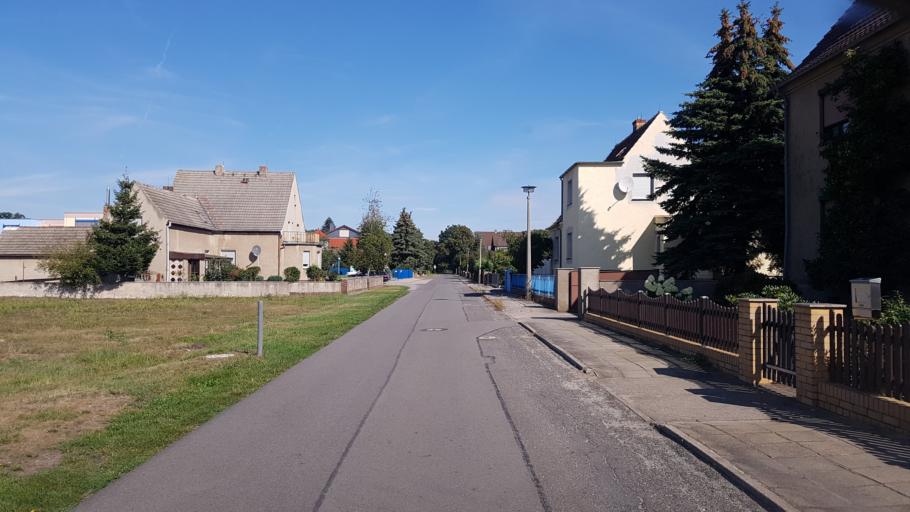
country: DE
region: Brandenburg
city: Plessa
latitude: 51.4672
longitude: 13.6264
